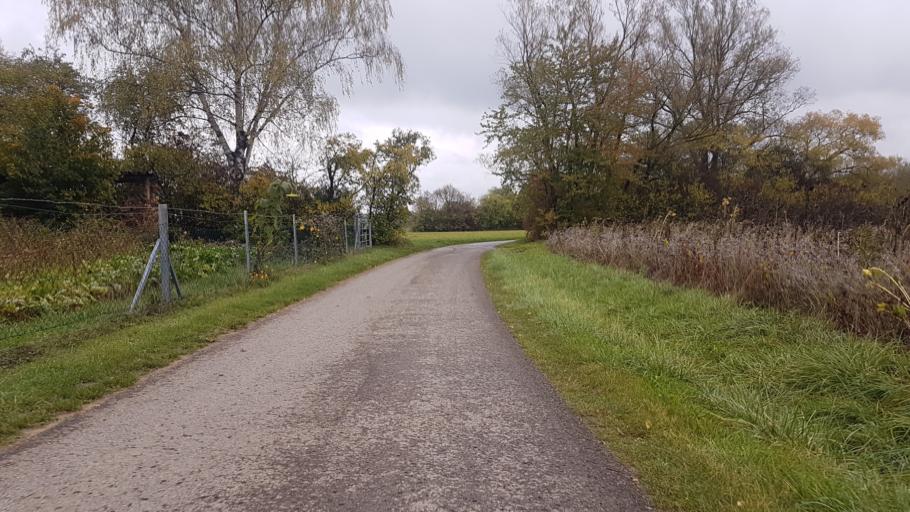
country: DE
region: Baden-Wuerttemberg
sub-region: Tuebingen Region
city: Ofterdingen
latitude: 48.4271
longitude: 9.0372
